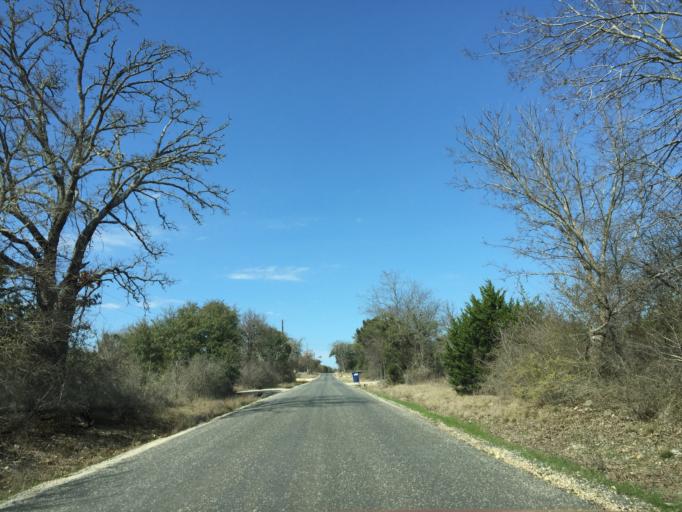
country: US
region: Texas
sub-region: Burnet County
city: Bertram
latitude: 30.7636
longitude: -97.9389
